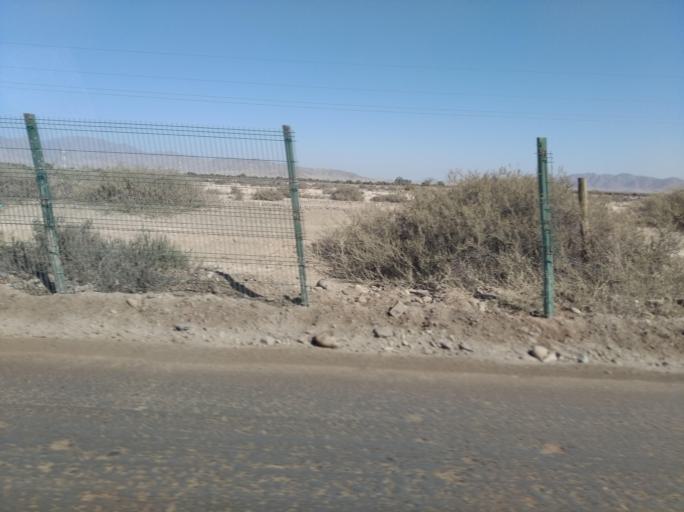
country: CL
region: Atacama
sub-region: Provincia de Copiapo
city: Copiapo
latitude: -27.3547
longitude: -70.6594
